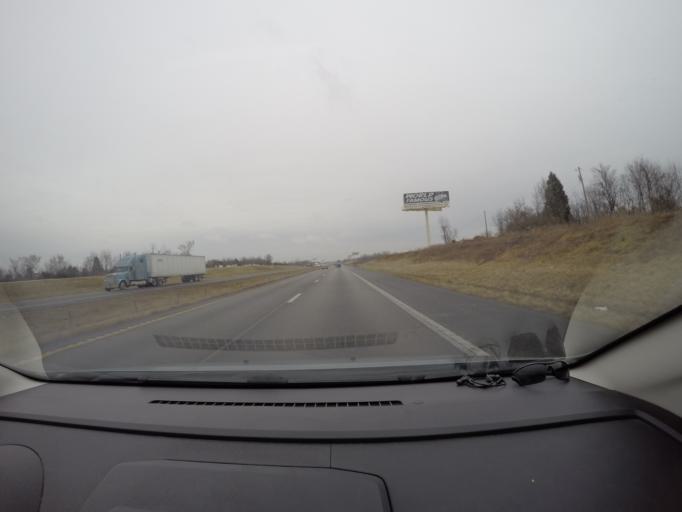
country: US
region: Missouri
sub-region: Warren County
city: Warrenton
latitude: 38.8635
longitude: -91.3227
